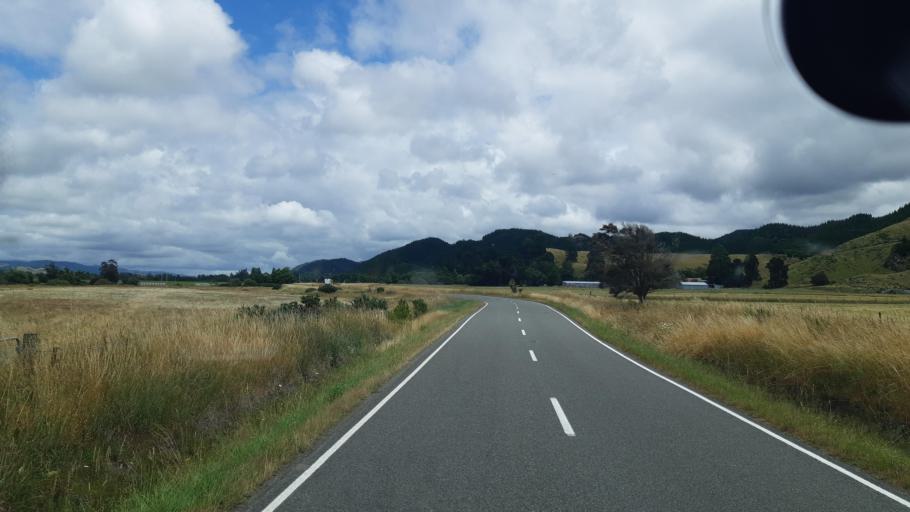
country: NZ
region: Marlborough
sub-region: Marlborough District
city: Blenheim
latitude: -41.4774
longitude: 173.7892
